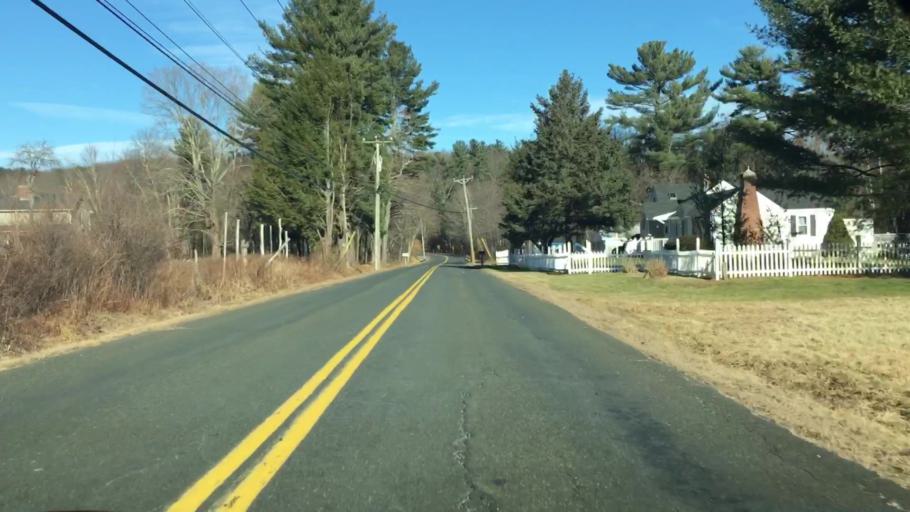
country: US
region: Connecticut
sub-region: Tolland County
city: Crystal Lake
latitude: 41.9307
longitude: -72.3876
